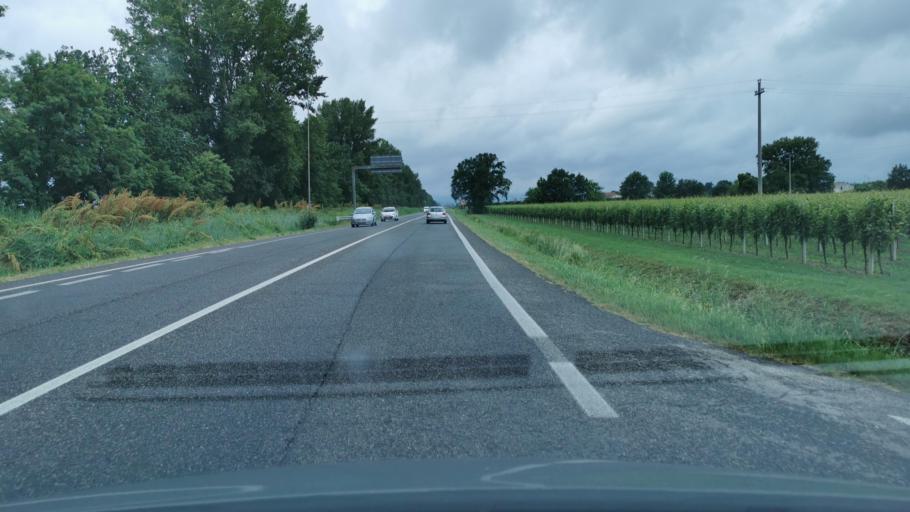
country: IT
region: Emilia-Romagna
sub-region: Provincia di Ravenna
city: Granarolo
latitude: 44.3494
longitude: 11.9265
